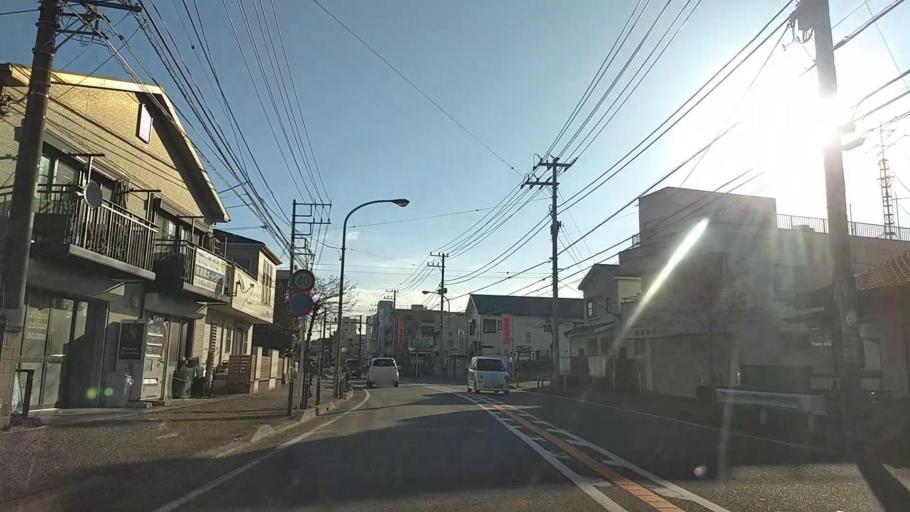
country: JP
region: Kanagawa
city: Fujisawa
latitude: 35.3469
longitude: 139.4706
